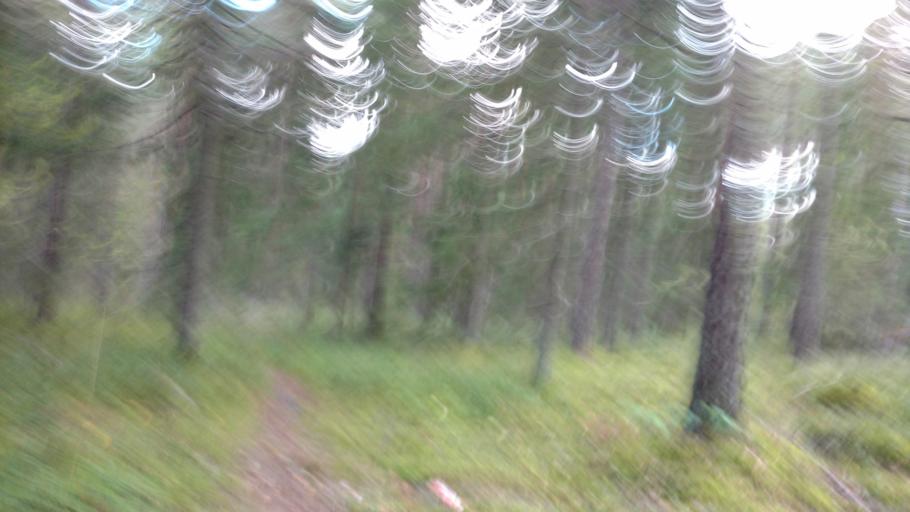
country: FI
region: Varsinais-Suomi
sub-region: Salo
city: Salo
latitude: 60.3577
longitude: 23.1644
